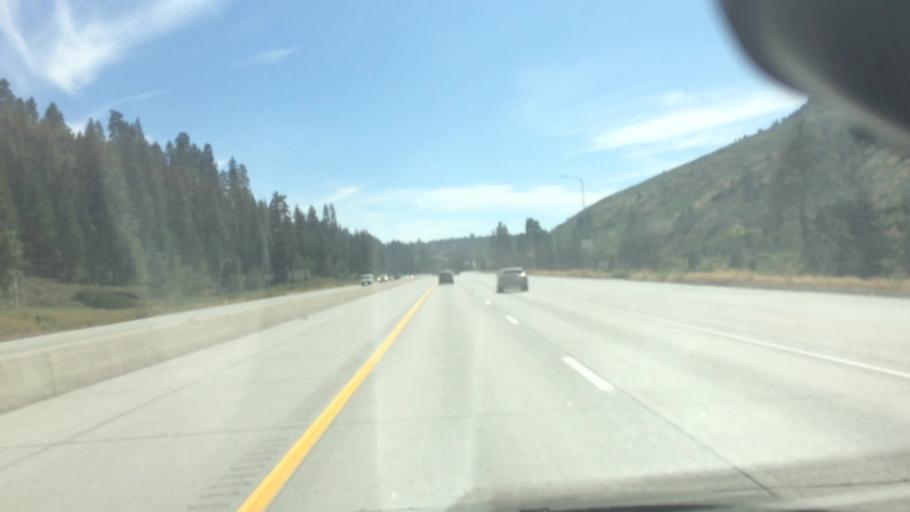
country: US
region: California
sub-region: Nevada County
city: Truckee
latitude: 39.3812
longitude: -120.0970
